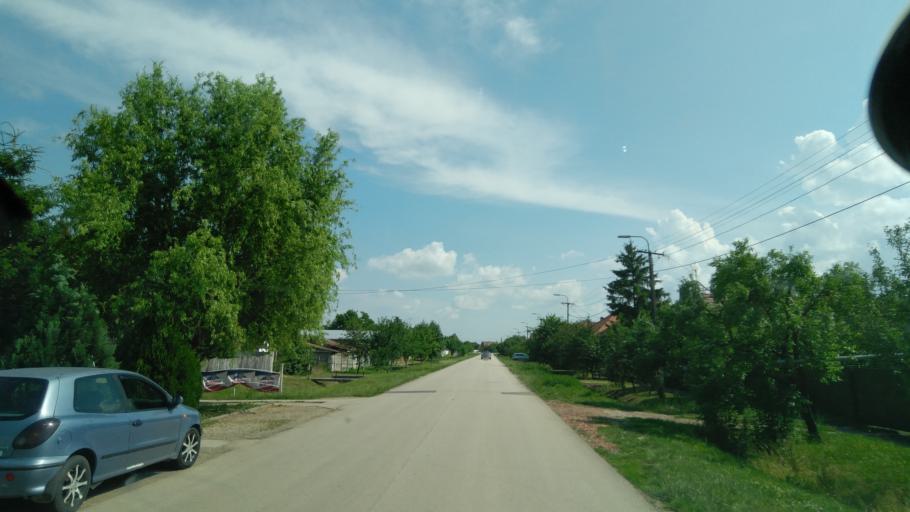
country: HU
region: Bekes
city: Doboz
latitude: 46.7363
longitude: 21.2372
